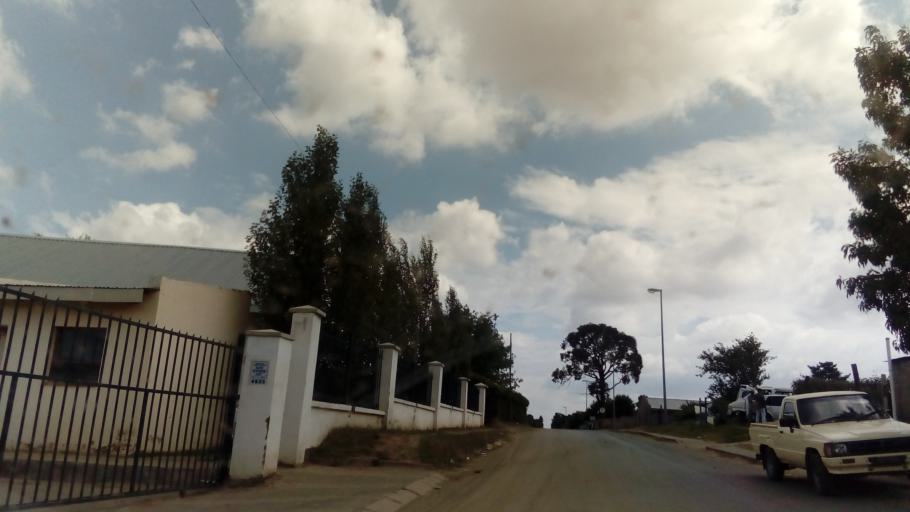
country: LS
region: Maseru
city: Maseru
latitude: -29.3716
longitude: 27.5317
